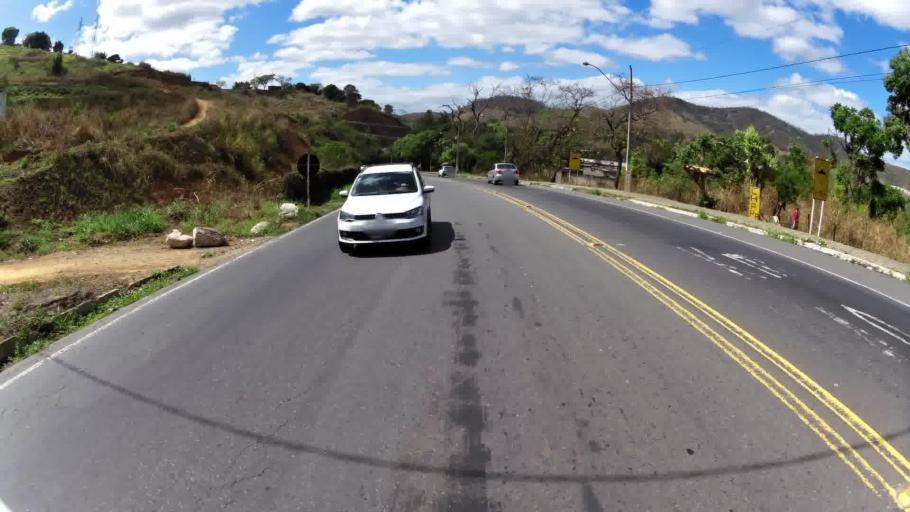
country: BR
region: Minas Gerais
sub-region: Alem Paraiba
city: Alem Paraiba
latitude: -21.8694
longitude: -42.6705
